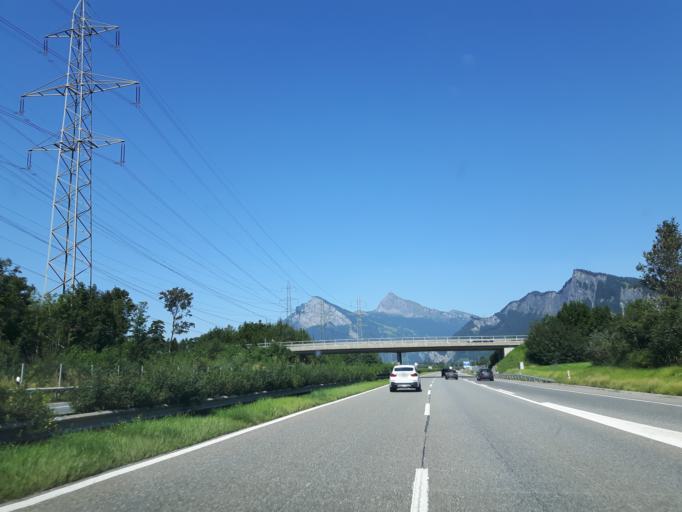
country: CH
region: Grisons
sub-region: Landquart District
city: Maienfeld
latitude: 47.0007
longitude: 9.5218
